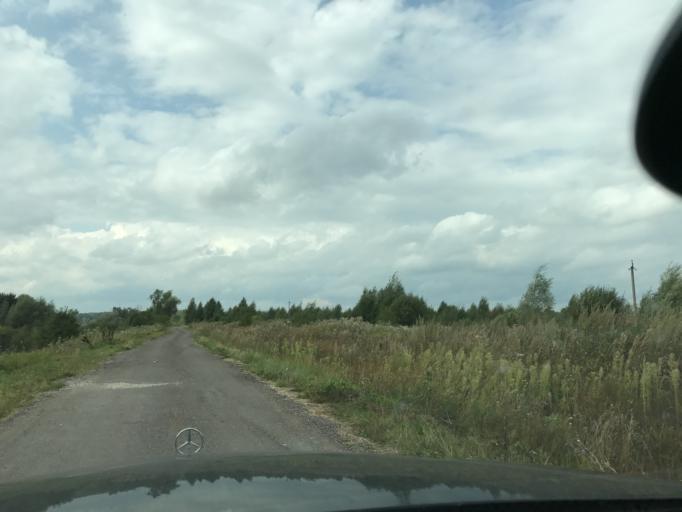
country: RU
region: Nizjnij Novgorod
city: Vacha
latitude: 55.9783
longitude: 42.7713
